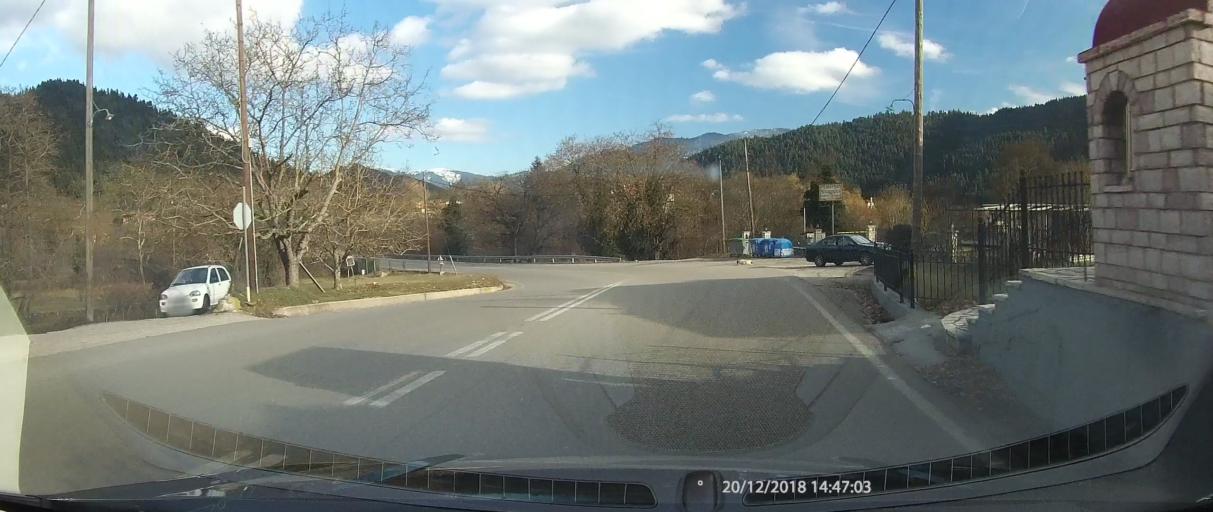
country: GR
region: Central Greece
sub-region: Nomos Evrytanias
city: Karpenisi
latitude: 38.9007
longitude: 21.7734
